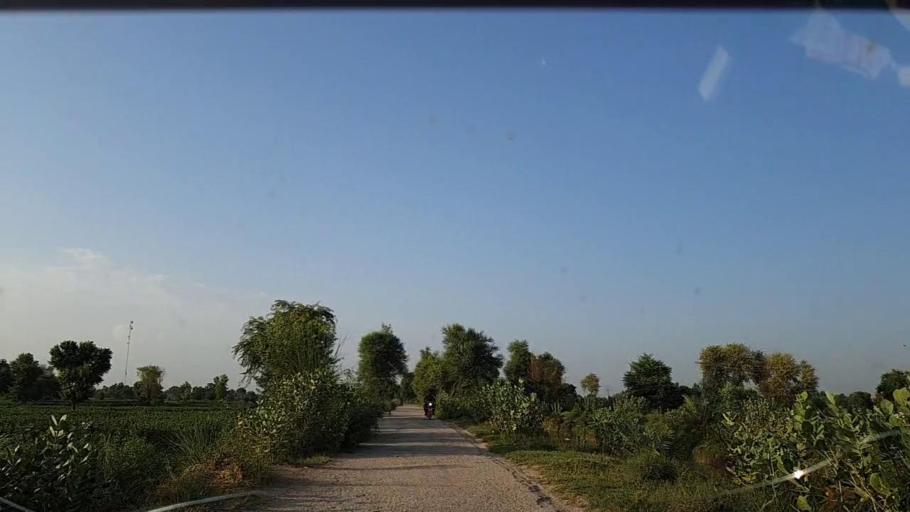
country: PK
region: Sindh
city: Pano Aqil
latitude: 27.9118
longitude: 69.2002
